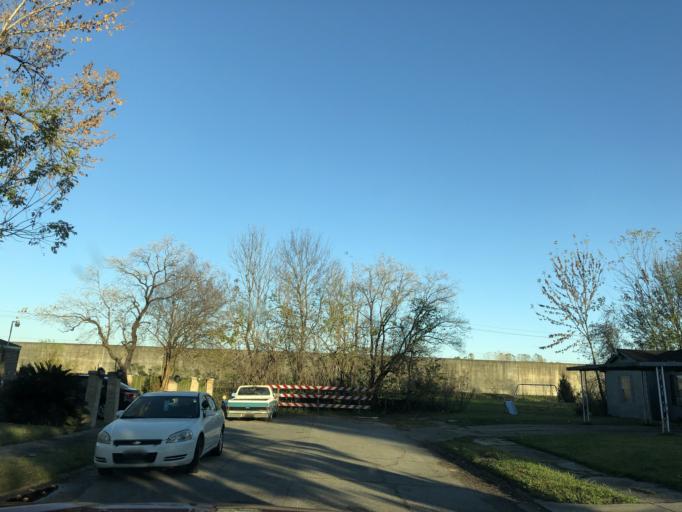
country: US
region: Texas
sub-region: Harris County
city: Jacinto City
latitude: 29.7619
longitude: -95.2665
